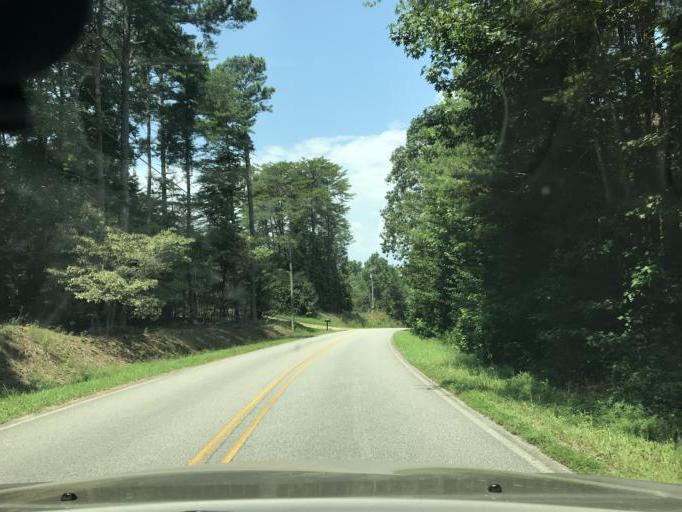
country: US
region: Georgia
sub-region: Dawson County
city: Dawsonville
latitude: 34.3456
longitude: -84.0848
